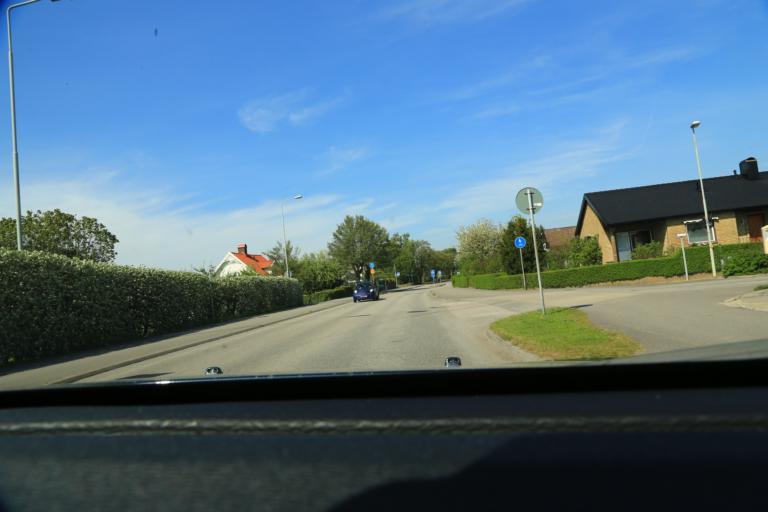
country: SE
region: Halland
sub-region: Varbergs Kommun
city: Varberg
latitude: 57.1264
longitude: 12.2680
